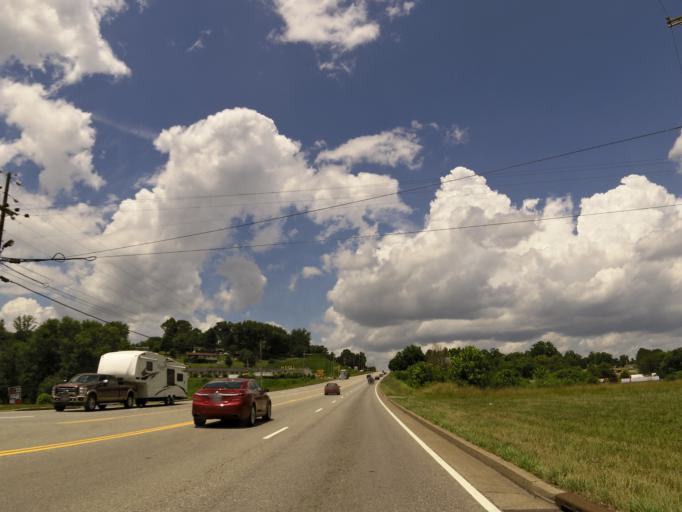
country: US
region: Tennessee
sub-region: Claiborne County
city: Tazewell
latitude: 36.4621
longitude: -83.5705
